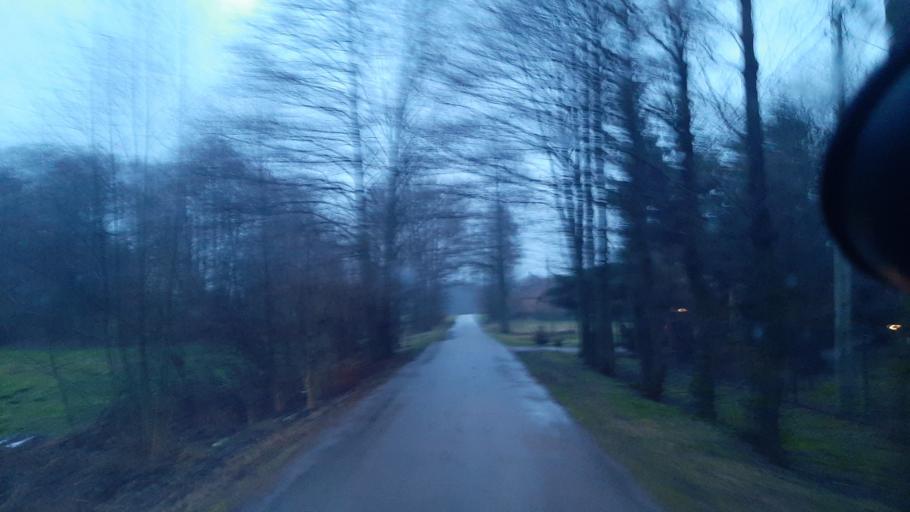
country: PL
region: Lublin Voivodeship
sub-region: Powiat lubelski
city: Jastkow
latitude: 51.3882
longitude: 22.4139
